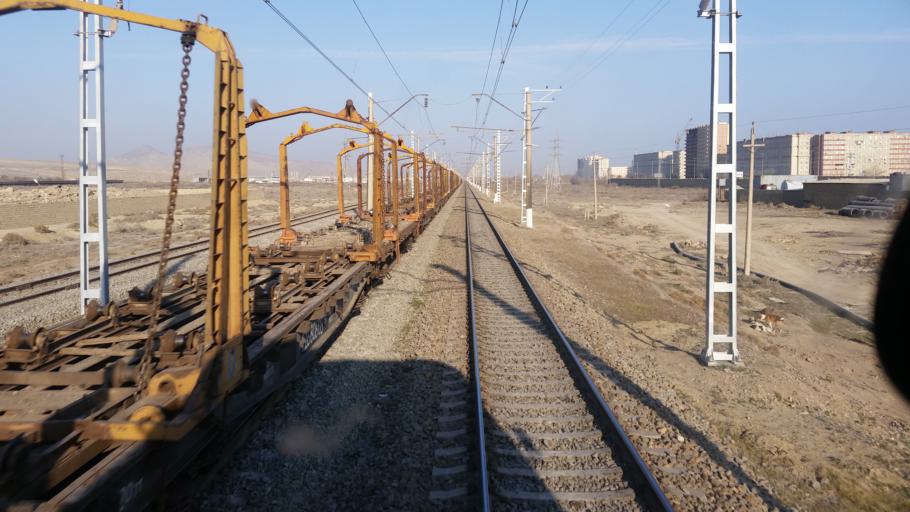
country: AZ
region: Baki
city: Korgoz
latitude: 40.2264
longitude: 49.5664
